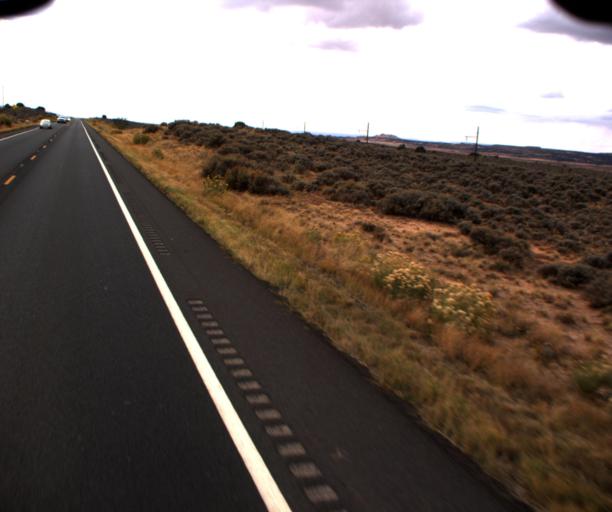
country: US
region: Arizona
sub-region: Navajo County
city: Kayenta
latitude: 36.5412
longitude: -110.5478
